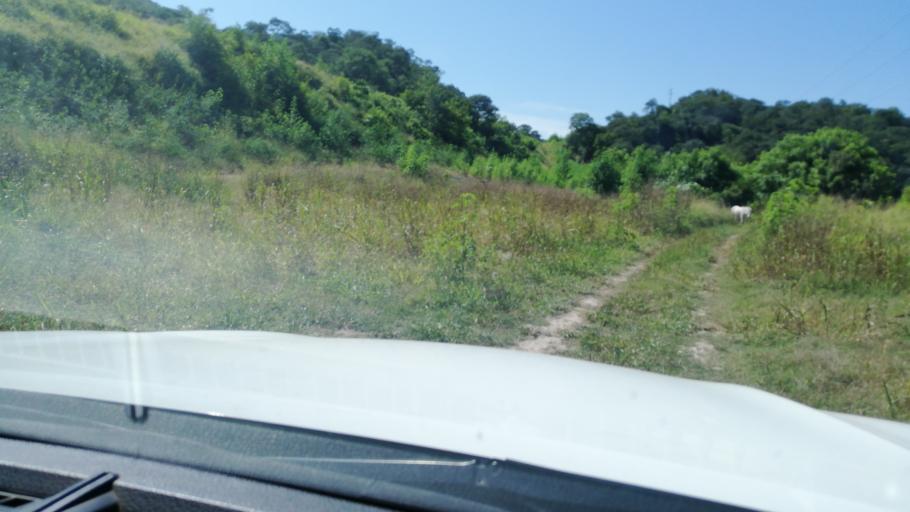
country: AR
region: Jujuy
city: La Mendieta
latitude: -24.3795
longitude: -65.0487
